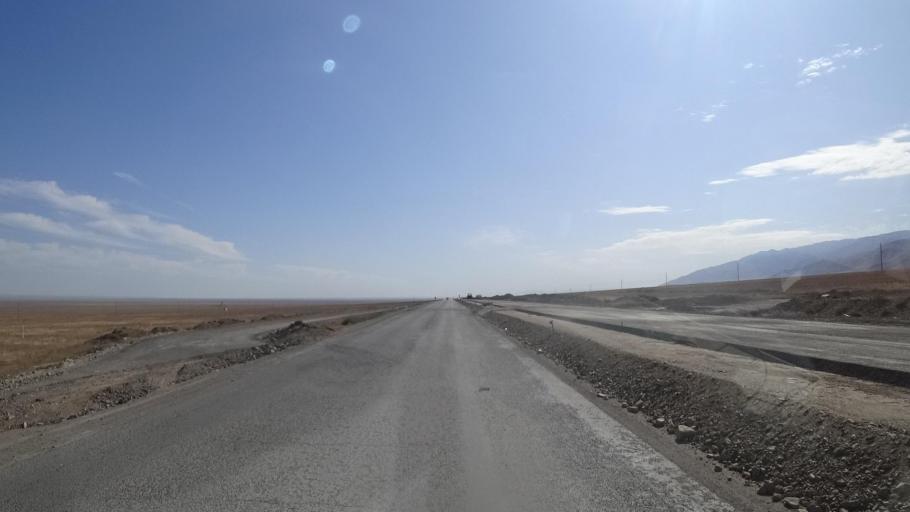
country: KG
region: Chuy
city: Ivanovka
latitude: 43.3831
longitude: 75.1850
